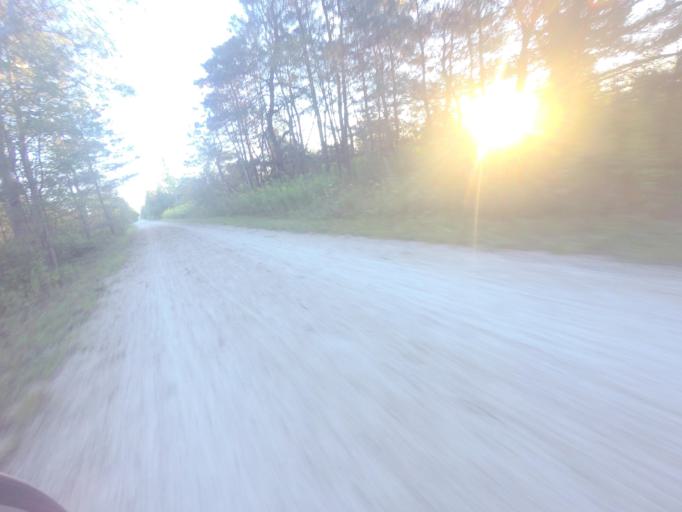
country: CA
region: Ontario
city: Bradford West Gwillimbury
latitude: 43.9761
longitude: -79.8071
